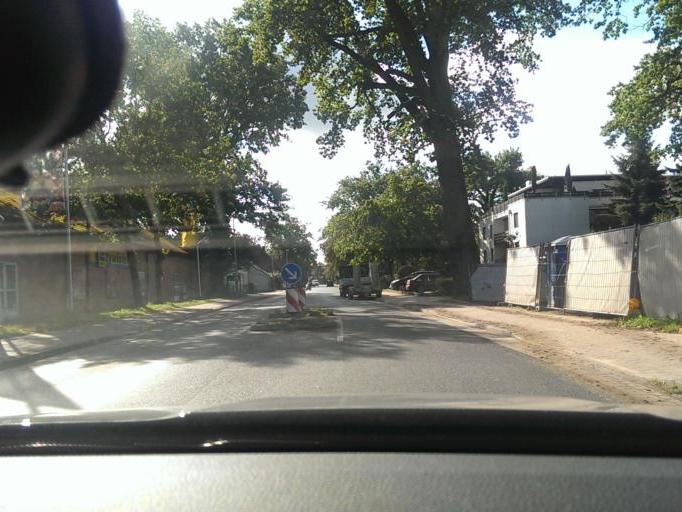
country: DE
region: Lower Saxony
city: Isernhagen Farster Bauerschaft
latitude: 52.4946
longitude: 9.8482
